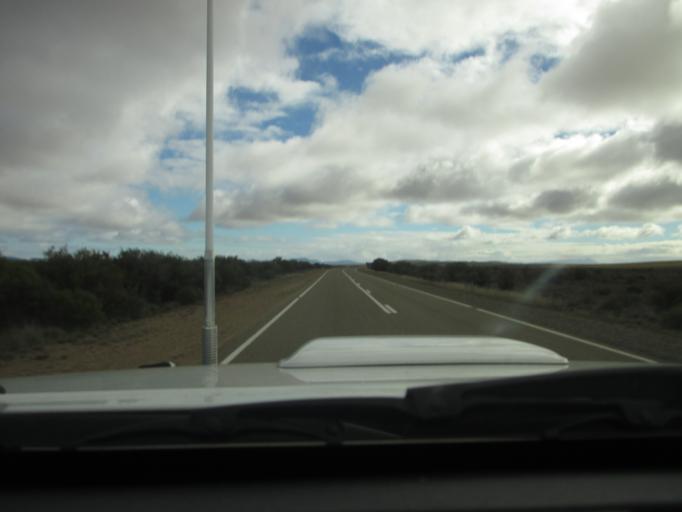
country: AU
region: South Australia
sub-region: Flinders Ranges
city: Quorn
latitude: -32.1230
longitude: 138.5077
